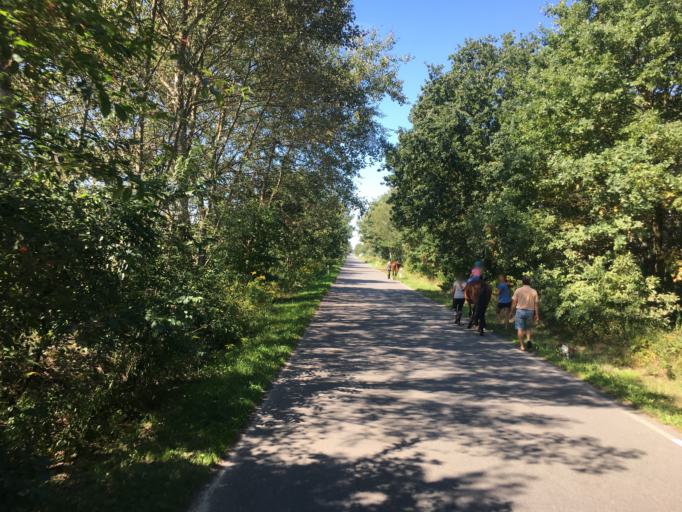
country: DE
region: Brandenburg
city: Welzow
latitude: 51.5254
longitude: 14.1769
